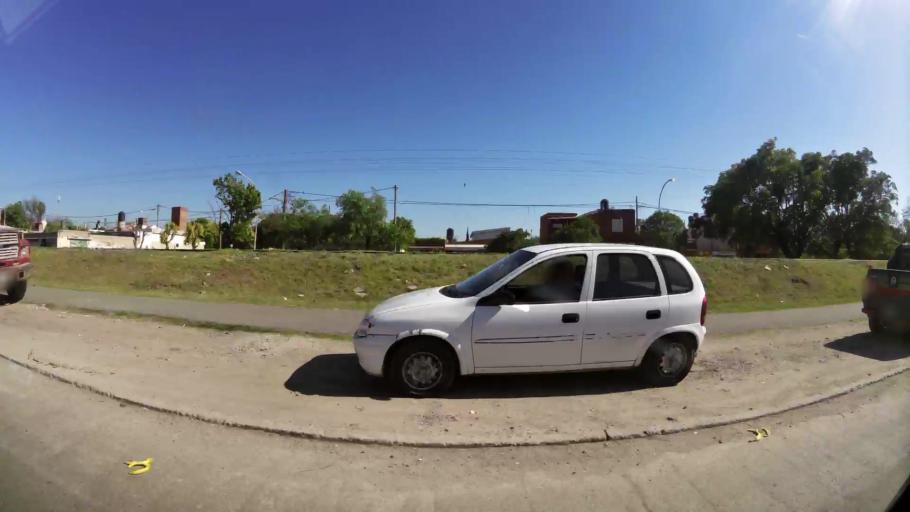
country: AR
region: Cordoba
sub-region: Departamento de Capital
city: Cordoba
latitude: -31.4404
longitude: -64.1666
